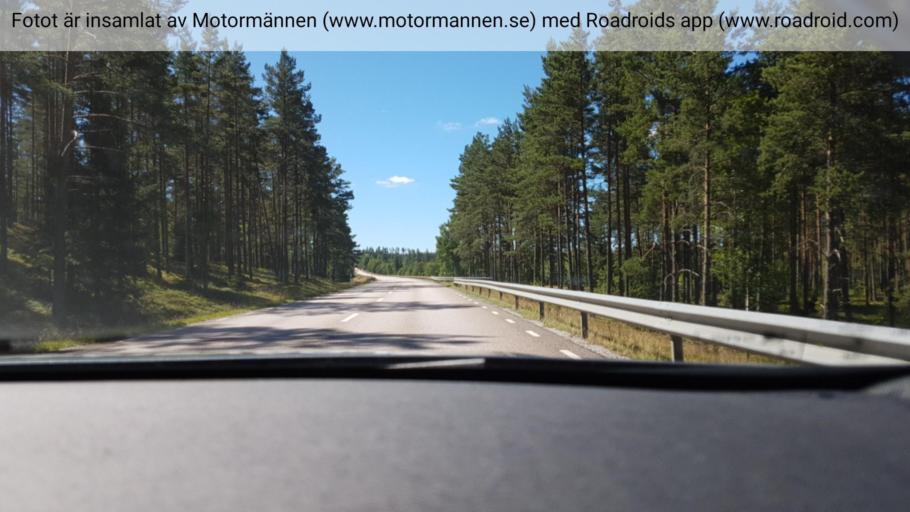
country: SE
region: Joenkoeping
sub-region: Mullsjo Kommun
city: Mullsjoe
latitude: 58.0500
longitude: 13.8509
